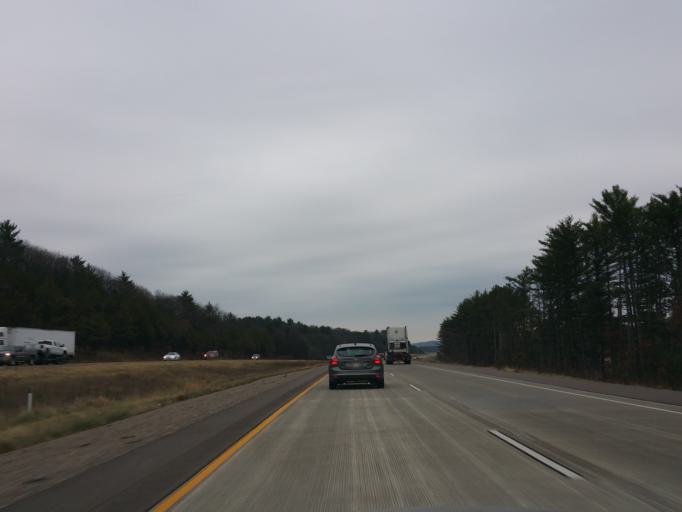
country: US
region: Wisconsin
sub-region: Jackson County
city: Black River Falls
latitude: 44.3313
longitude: -90.8951
